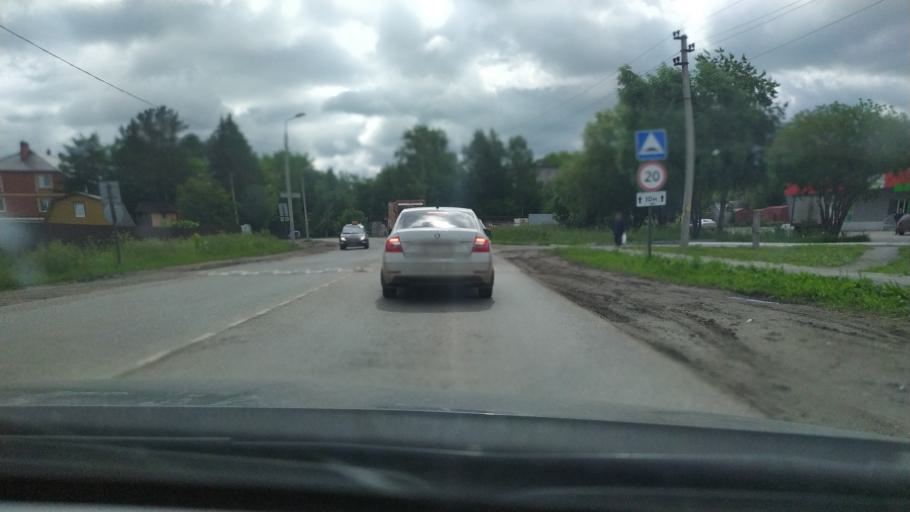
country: RU
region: Perm
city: Froly
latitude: 57.9764
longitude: 56.3154
